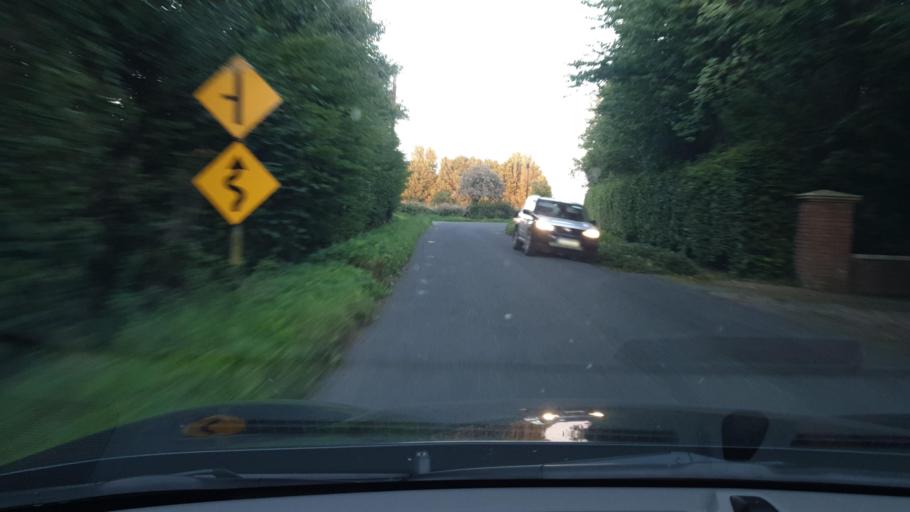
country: IE
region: Leinster
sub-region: Kildare
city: Prosperous
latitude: 53.3255
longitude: -6.7904
